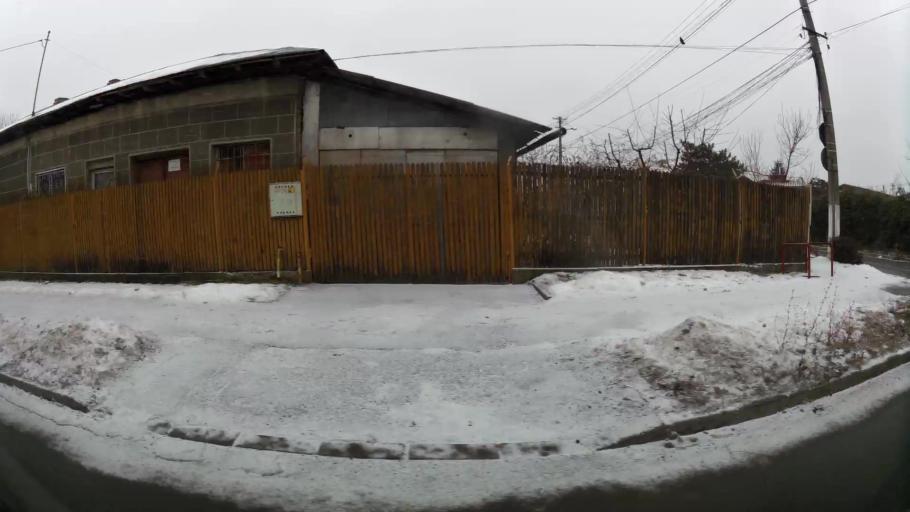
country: RO
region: Prahova
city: Ploiesti
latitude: 44.9527
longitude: 26.0402
